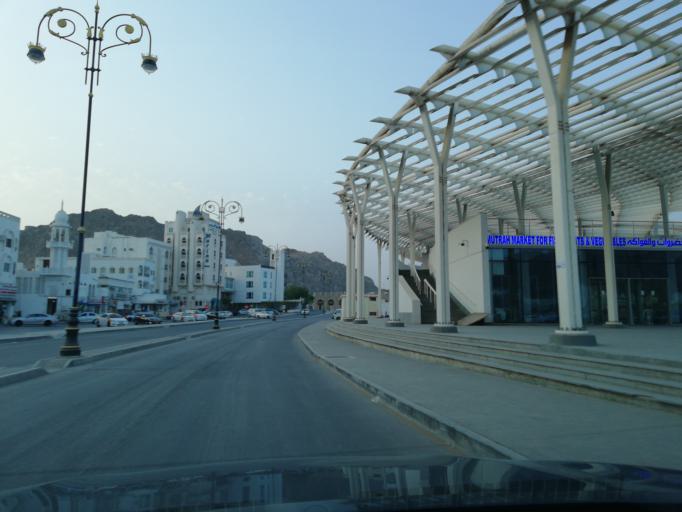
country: OM
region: Muhafazat Masqat
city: Muscat
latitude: 23.6242
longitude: 58.5616
